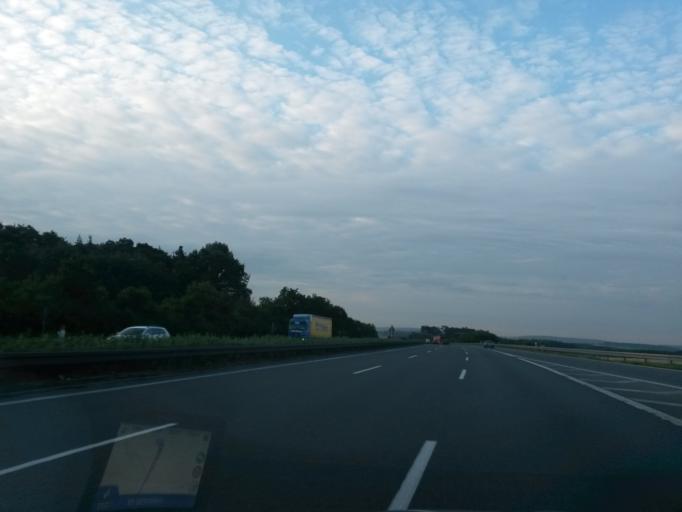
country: DE
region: Bavaria
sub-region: Regierungsbezirk Mittelfranken
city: Allersberg
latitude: 49.2175
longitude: 11.2263
